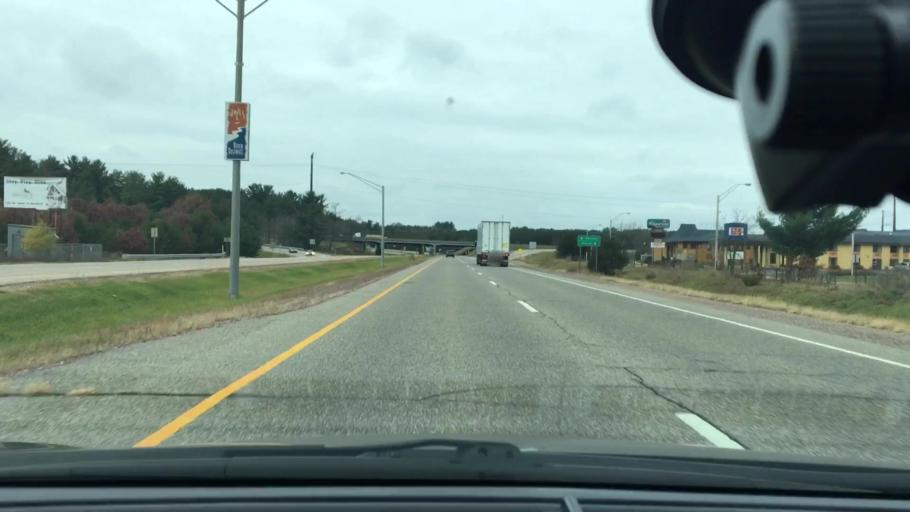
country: US
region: Wisconsin
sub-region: Sauk County
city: Lake Delton
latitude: 43.6244
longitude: -89.7984
